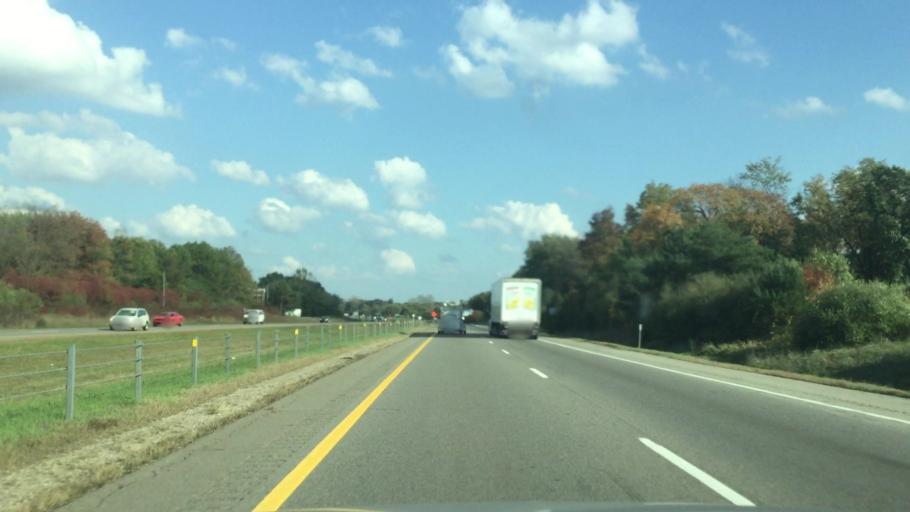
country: US
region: Michigan
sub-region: Calhoun County
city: Brownlee Park
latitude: 42.2990
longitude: -85.0727
